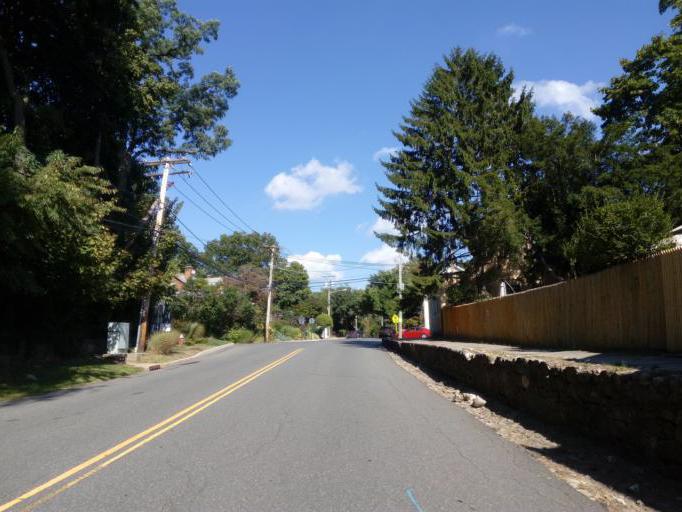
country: US
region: New York
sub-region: Nassau County
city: Glen Cove
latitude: 40.8665
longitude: -73.6474
